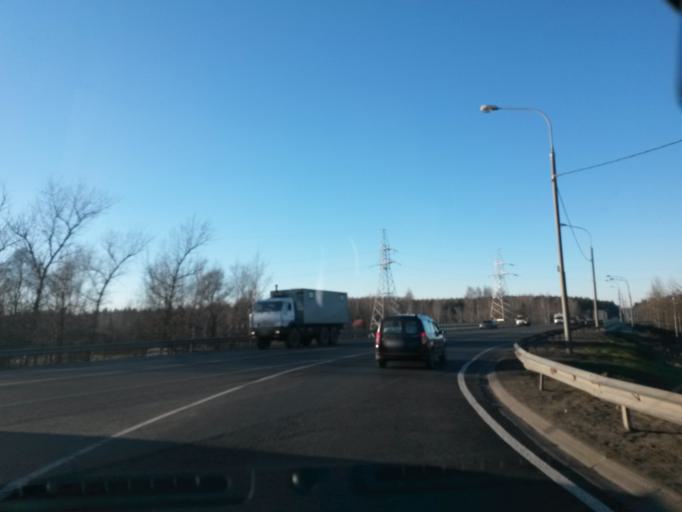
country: RU
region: Moskovskaya
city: Zelenogradskiy
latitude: 56.1061
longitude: 37.9615
